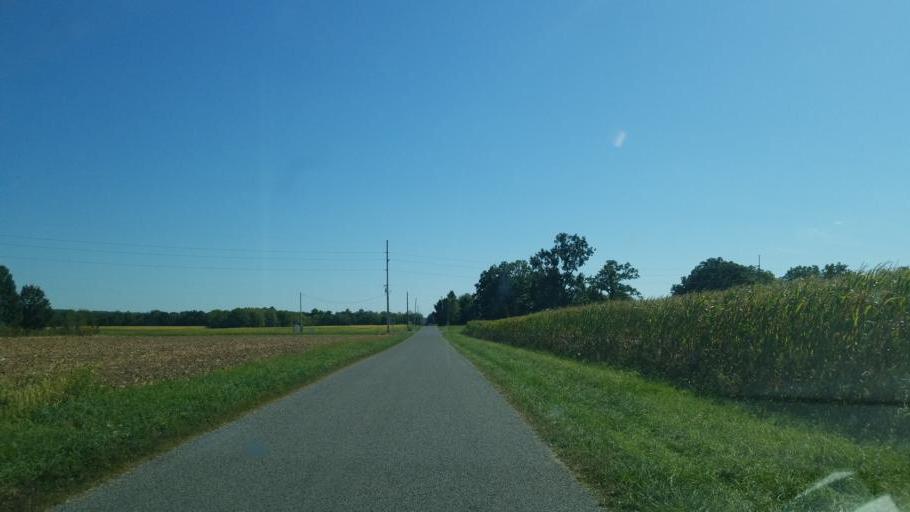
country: US
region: Ohio
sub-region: Logan County
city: West Liberty
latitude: 40.2796
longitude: -83.7048
